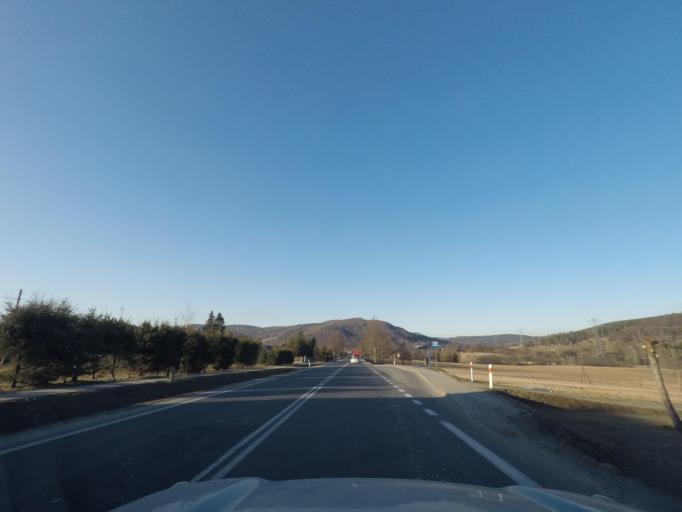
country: PL
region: Subcarpathian Voivodeship
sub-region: Powiat krosnienski
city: Dukla
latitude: 49.4552
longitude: 21.6932
